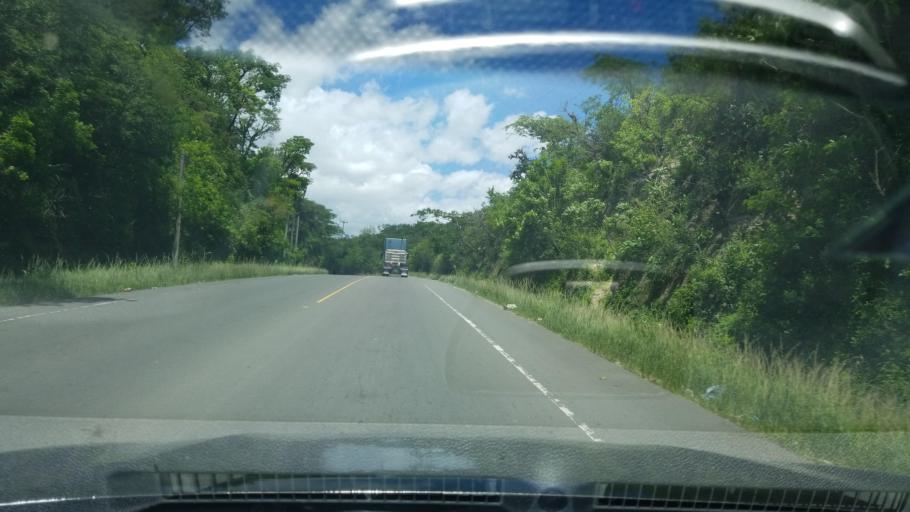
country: HN
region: Francisco Morazan
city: Rio Abajo
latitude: 14.1801
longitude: -87.2052
